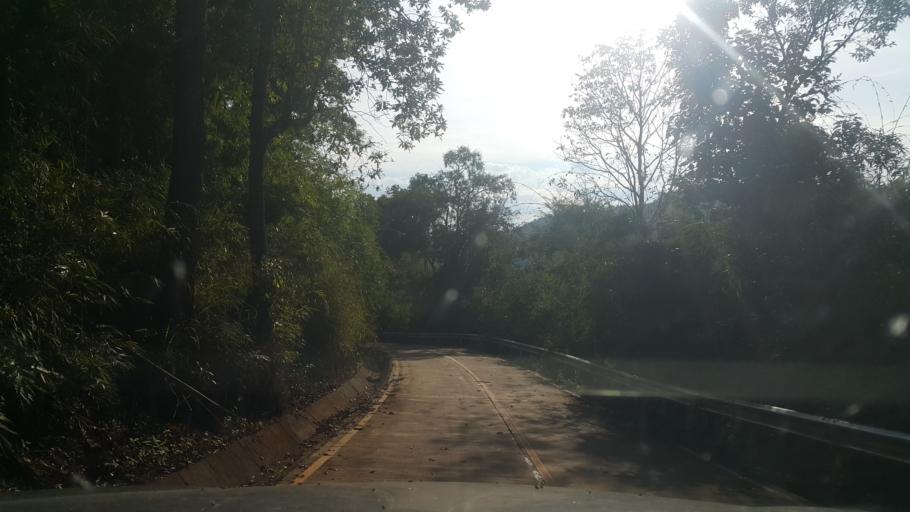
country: TH
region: Chiang Mai
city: Samoeng
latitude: 18.9991
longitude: 98.6807
